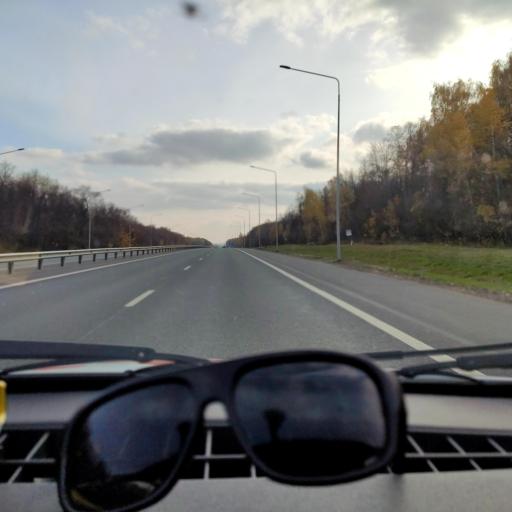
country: RU
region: Bashkortostan
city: Karmaskaly
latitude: 54.3978
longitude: 55.9176
